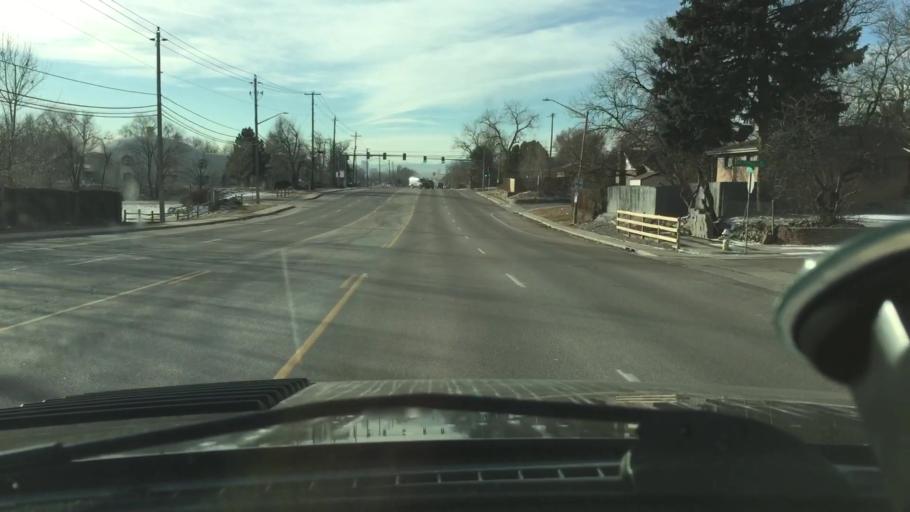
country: US
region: Colorado
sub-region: Adams County
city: Sherrelwood
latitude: 39.8437
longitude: -105.0061
